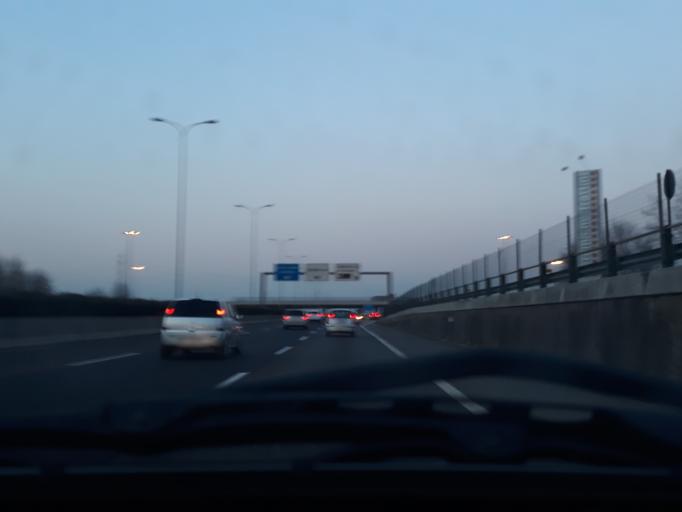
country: IT
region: Lombardy
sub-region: Provincia di Monza e Brianza
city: Santa Margherita
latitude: 45.6247
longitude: 9.2246
